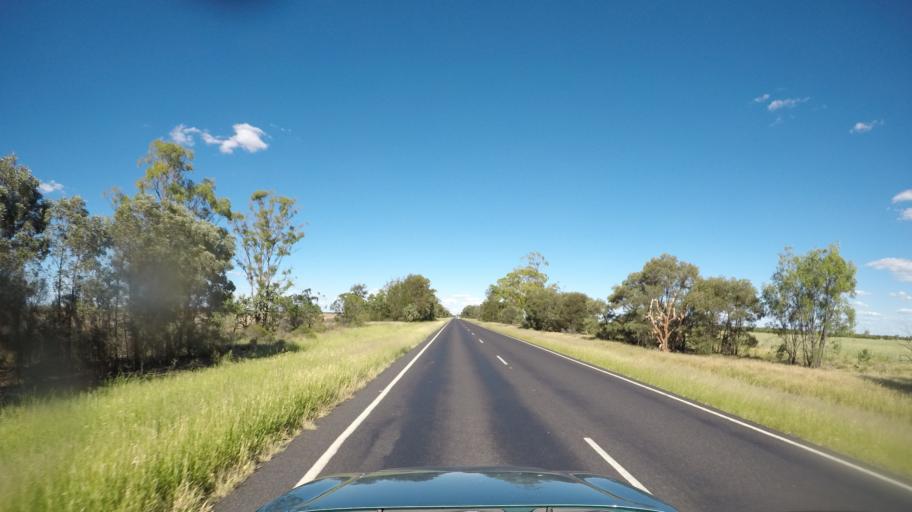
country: AU
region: Queensland
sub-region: Goondiwindi
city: Goondiwindi
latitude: -28.1688
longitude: 150.5154
